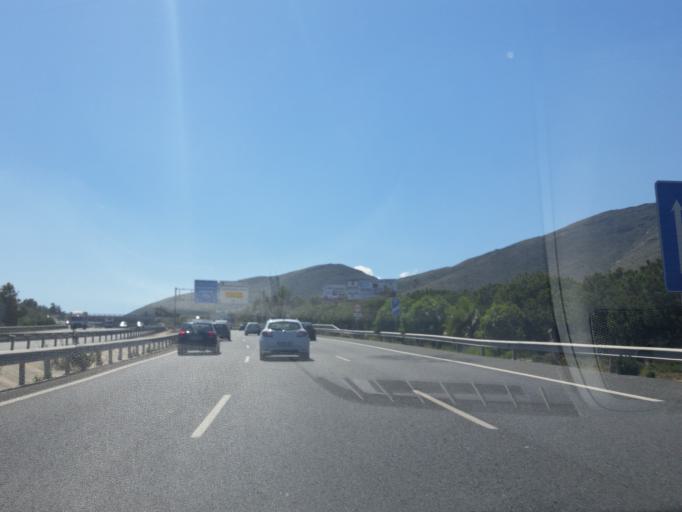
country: ES
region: Andalusia
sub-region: Provincia de Malaga
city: Torremolinos
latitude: 36.6416
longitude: -4.5071
